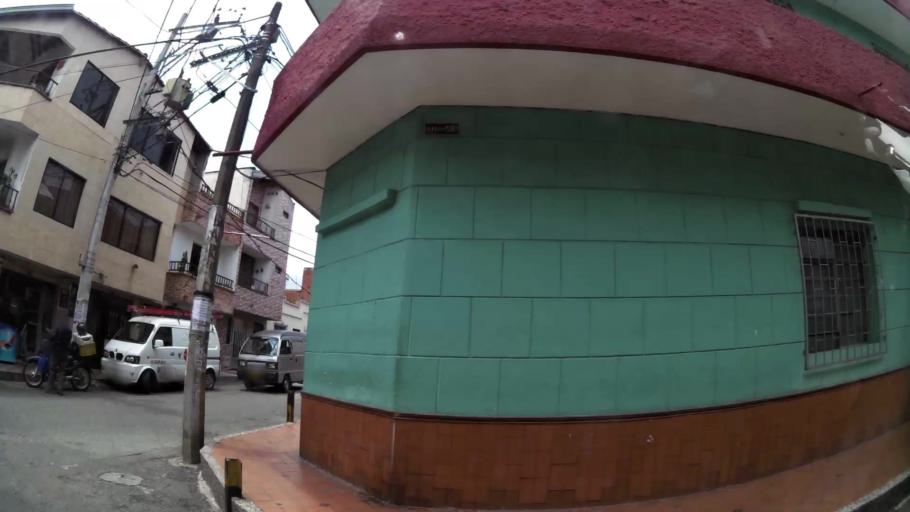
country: CO
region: Antioquia
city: Sabaneta
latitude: 6.1651
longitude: -75.6139
